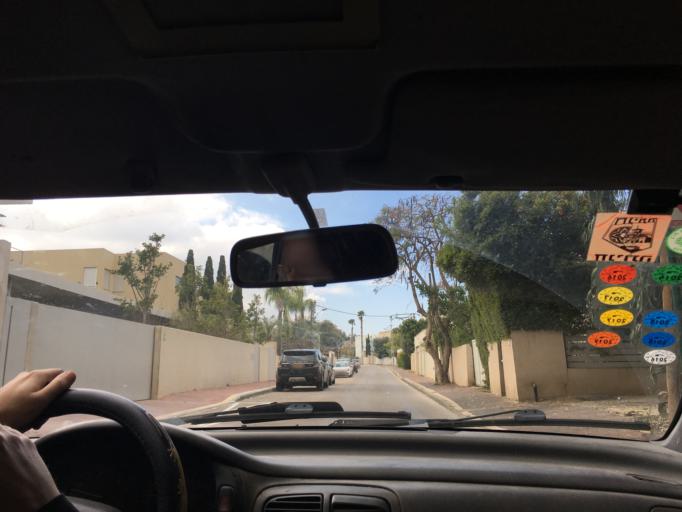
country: IL
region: Tel Aviv
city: Ramat HaSharon
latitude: 32.1456
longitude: 34.8315
